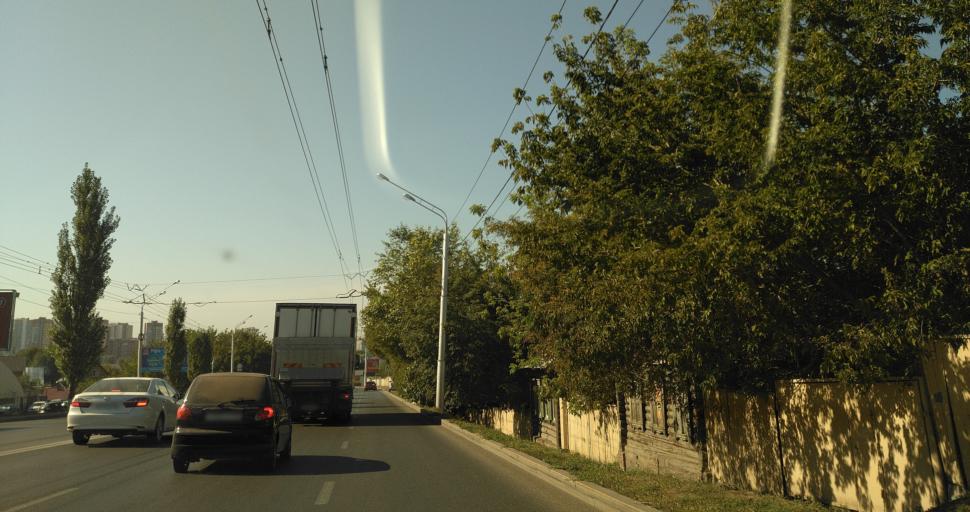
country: RU
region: Bashkortostan
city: Ufa
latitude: 54.7256
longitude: 55.9760
